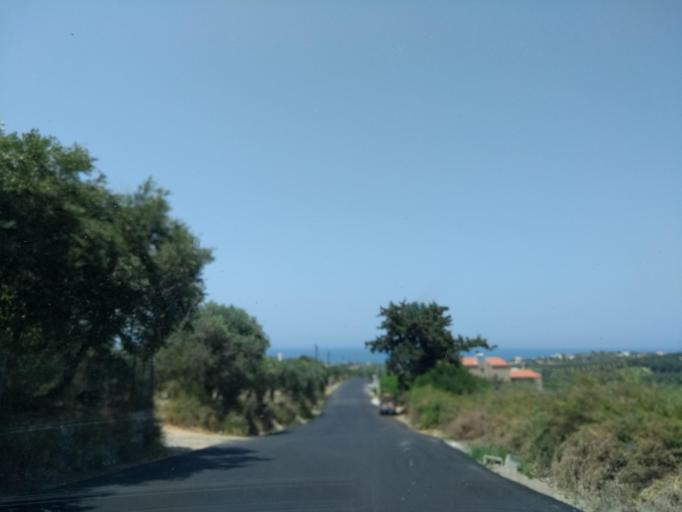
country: GR
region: Crete
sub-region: Nomos Chanias
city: Georgioupolis
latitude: 35.3326
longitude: 24.3016
